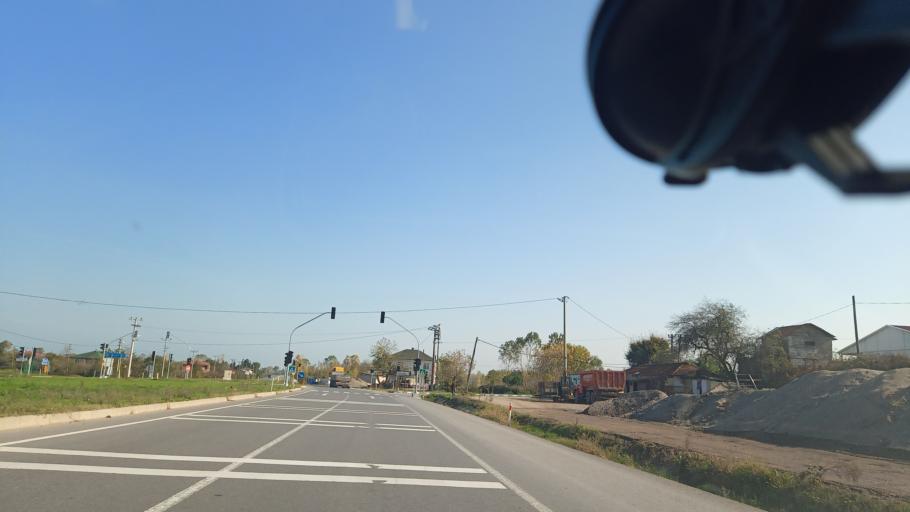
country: TR
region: Sakarya
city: Karasu
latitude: 41.0695
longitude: 30.8019
